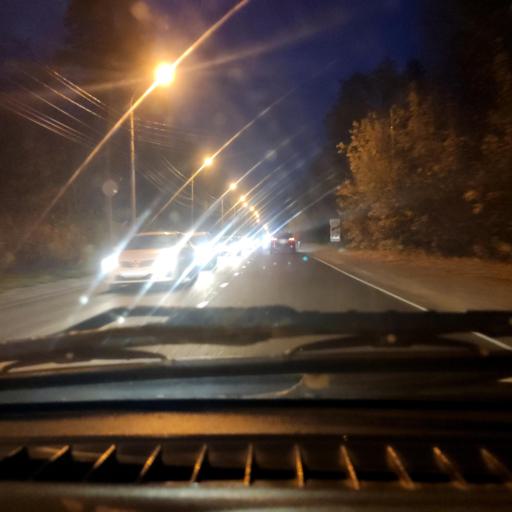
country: RU
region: Samara
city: Tol'yatti
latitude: 53.4934
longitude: 49.2956
